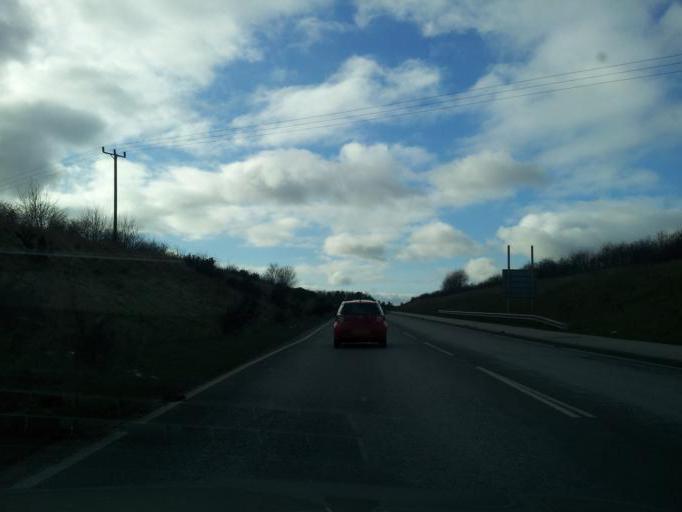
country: GB
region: England
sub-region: Nottinghamshire
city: Mansfield
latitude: 53.1182
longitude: -1.1902
